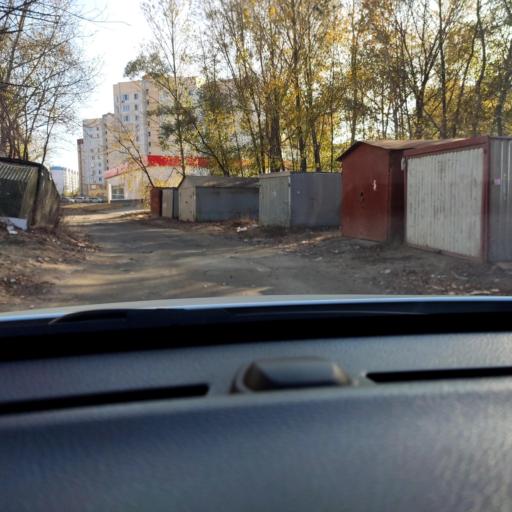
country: RU
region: Voronezj
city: Voronezh
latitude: 51.7210
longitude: 39.2619
